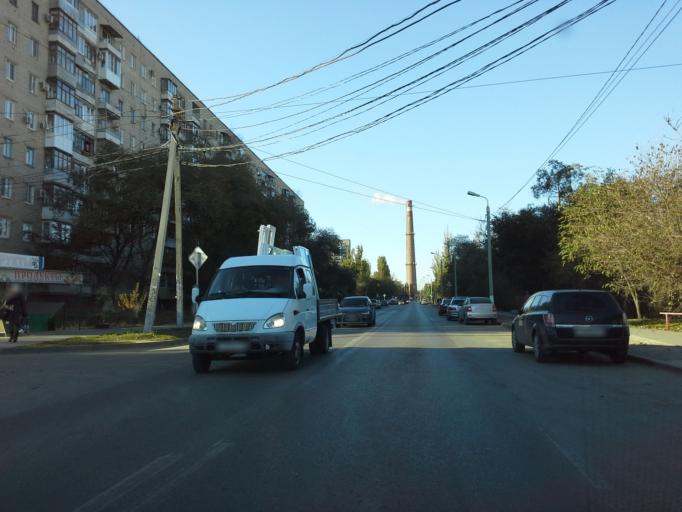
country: RU
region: Volgograd
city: Vodstroy
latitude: 48.8211
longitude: 44.6321
